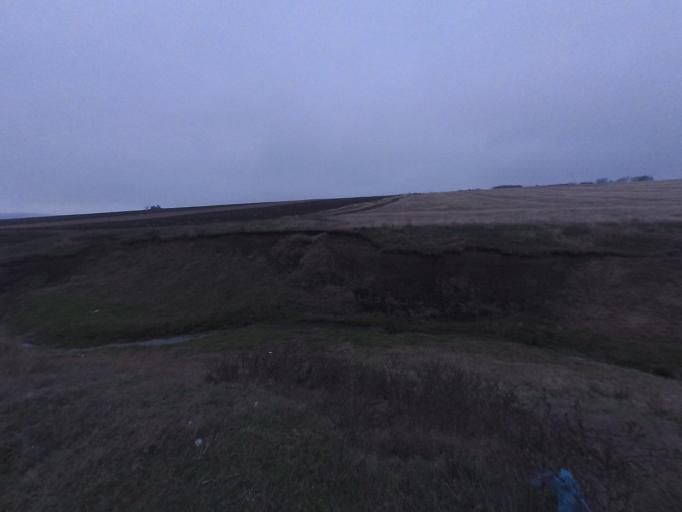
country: RO
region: Galati
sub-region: Comuna Balabanesti
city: Balabanesti
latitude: 46.1306
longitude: 27.7492
